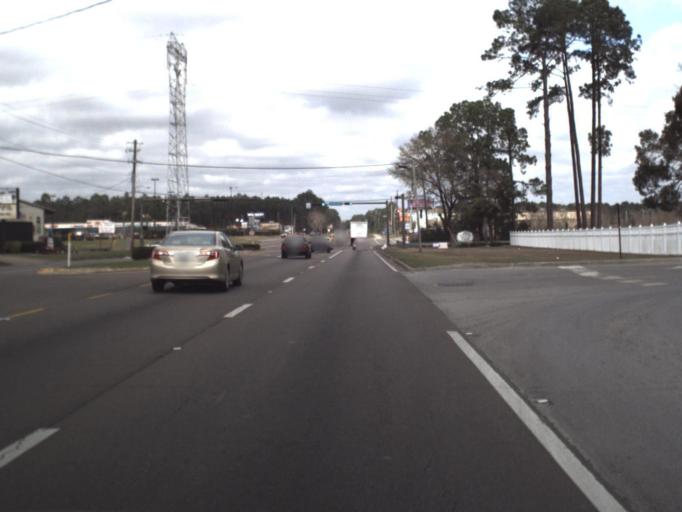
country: US
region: Florida
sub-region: Bay County
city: Springfield
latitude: 30.1590
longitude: -85.5910
